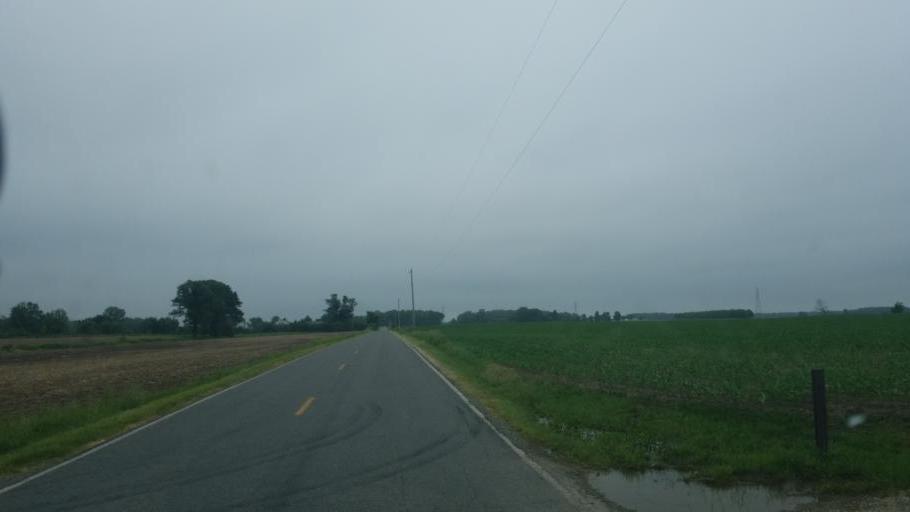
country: US
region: Indiana
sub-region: Marshall County
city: Bremen
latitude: 41.4899
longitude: -86.1179
